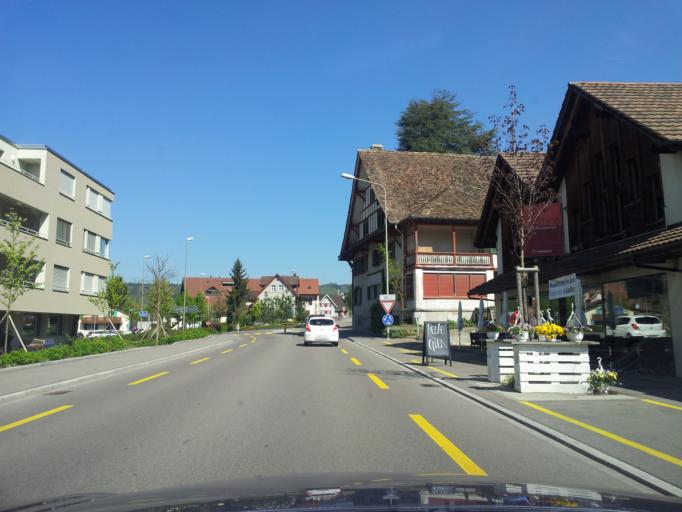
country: CH
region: Zurich
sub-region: Bezirk Affoltern
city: Hedingen
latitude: 47.2969
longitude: 8.4486
